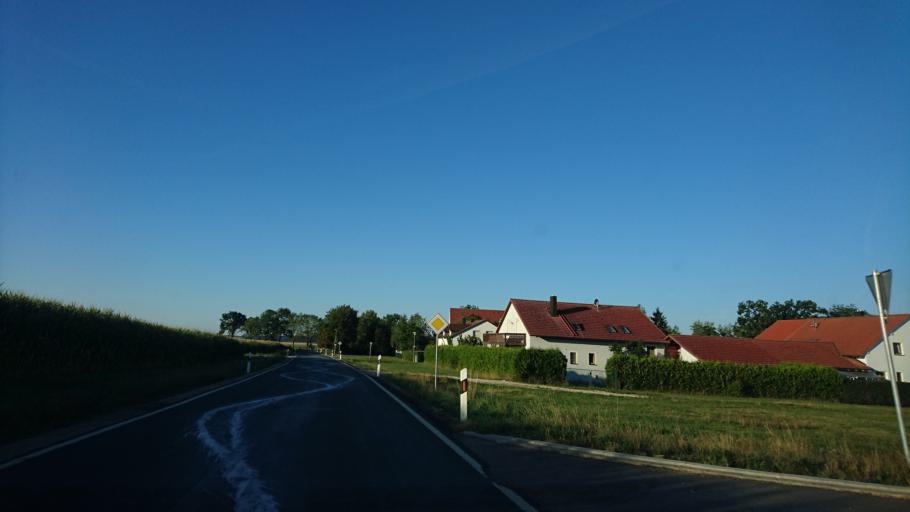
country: DE
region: Bavaria
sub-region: Regierungsbezirk Mittelfranken
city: Nennslingen
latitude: 49.0594
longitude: 11.1727
